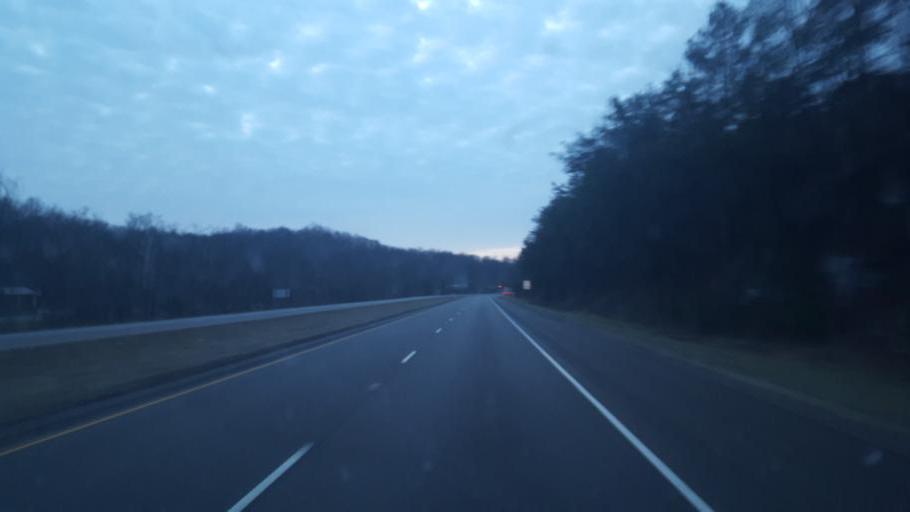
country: US
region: Ohio
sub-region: Jackson County
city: Oak Hill
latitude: 38.9234
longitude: -82.4642
